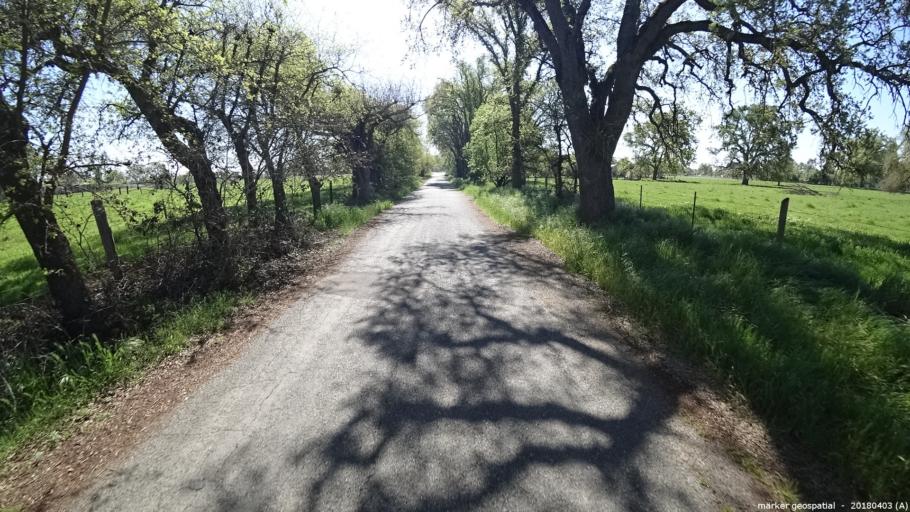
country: US
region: California
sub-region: Sacramento County
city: Wilton
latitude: 38.4298
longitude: -121.2070
